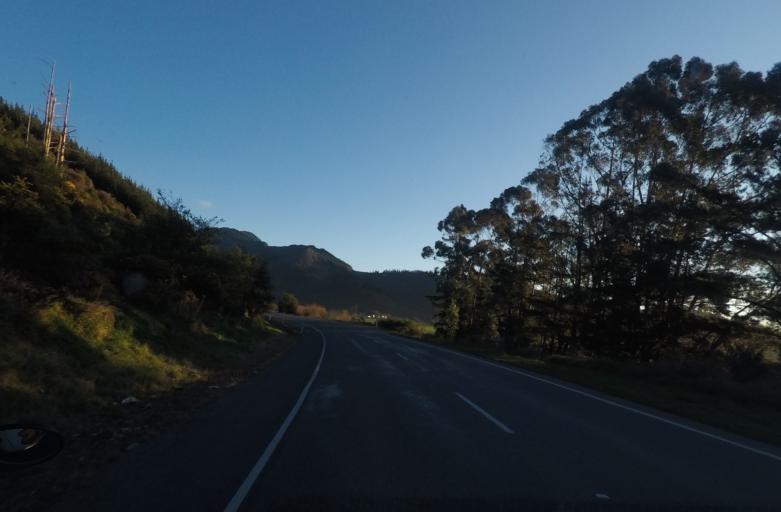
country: NZ
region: Marlborough
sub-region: Marlborough District
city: Picton
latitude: -41.2881
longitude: 173.6802
